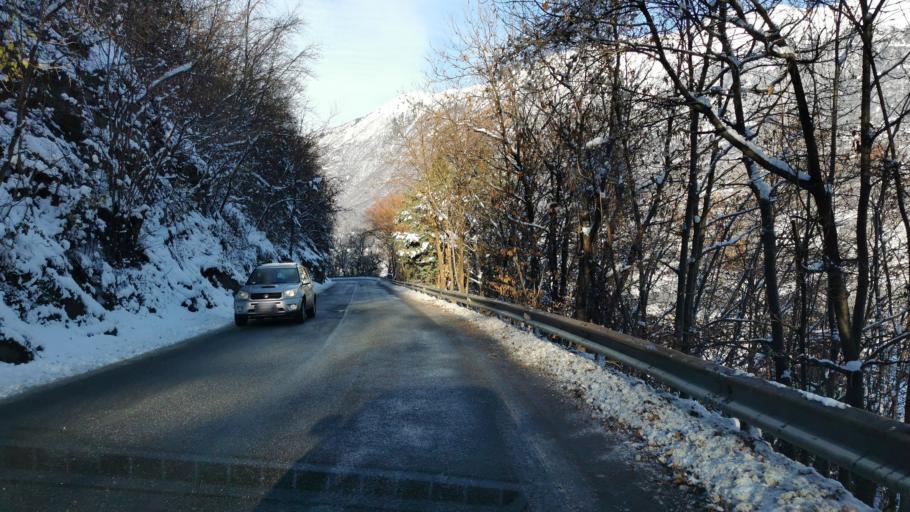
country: IT
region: Lombardy
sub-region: Provincia di Sondrio
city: Bema
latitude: 46.1221
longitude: 9.5595
